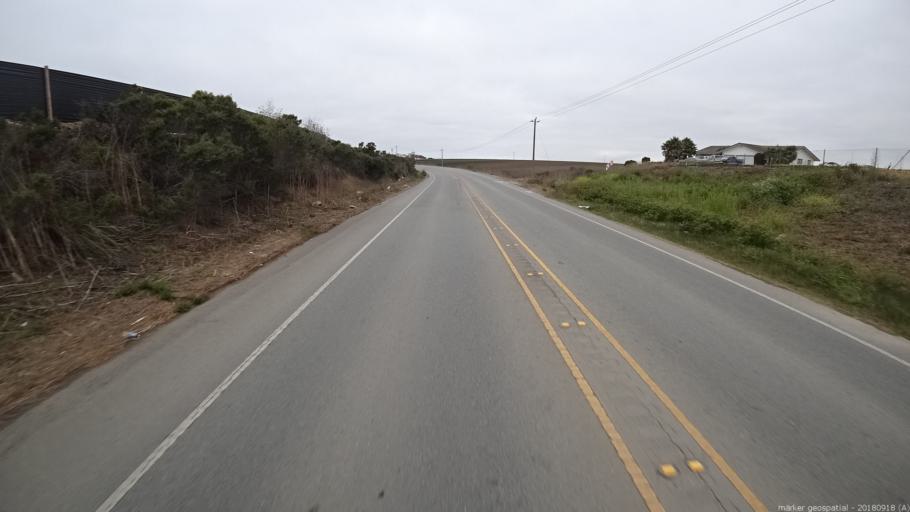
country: US
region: California
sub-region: Monterey County
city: Prunedale
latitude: 36.7458
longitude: -121.6953
